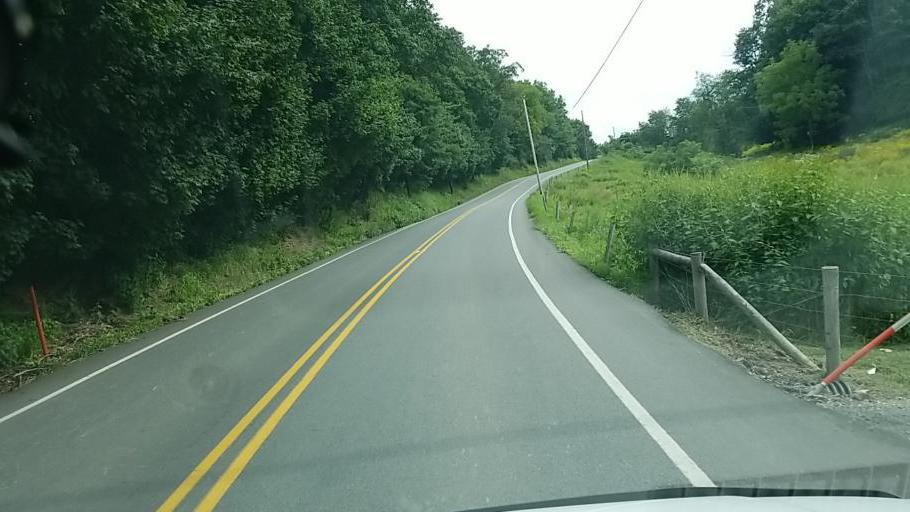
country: US
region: Pennsylvania
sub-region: Dauphin County
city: Elizabethville
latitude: 40.6185
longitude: -76.7843
